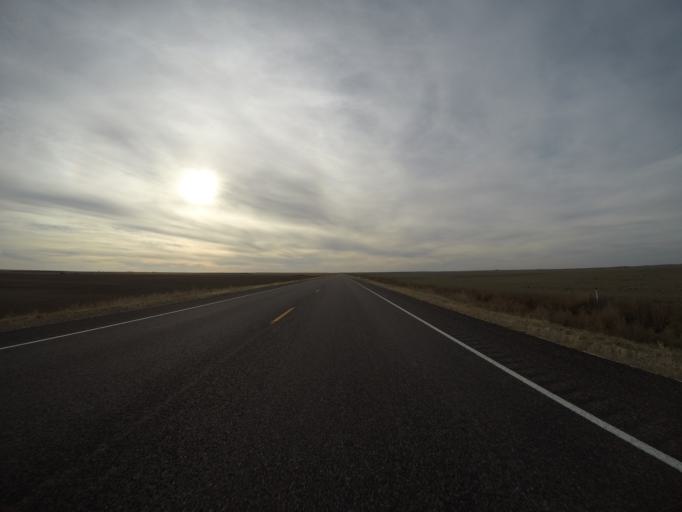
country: US
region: Kansas
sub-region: Cheyenne County
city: Saint Francis
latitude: 39.7464
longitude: -102.1014
